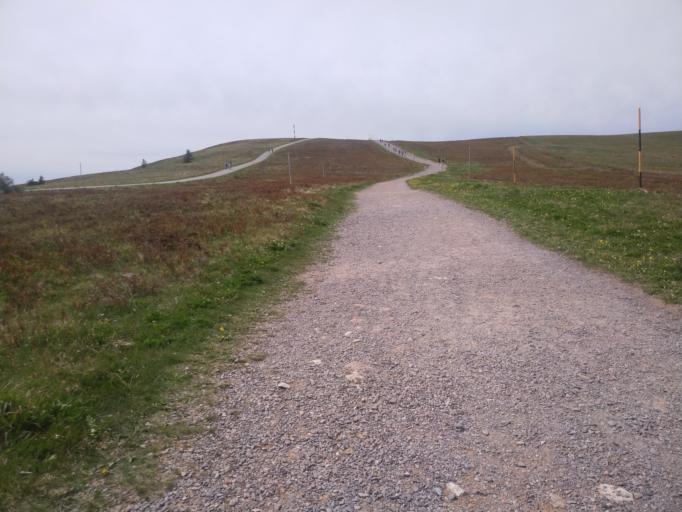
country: DE
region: Baden-Wuerttemberg
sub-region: Freiburg Region
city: Bernau
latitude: 47.8675
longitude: 8.0172
